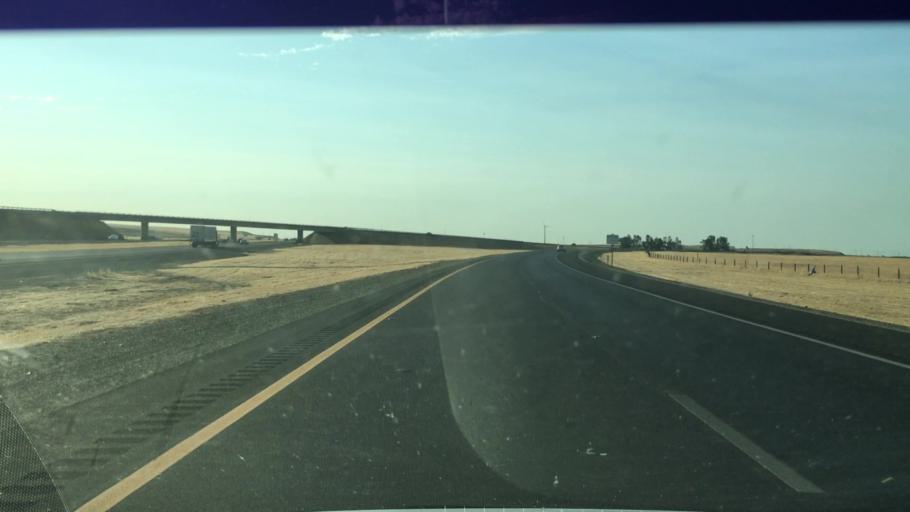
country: US
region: California
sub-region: San Joaquin County
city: Tracy
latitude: 37.5958
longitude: -121.3392
